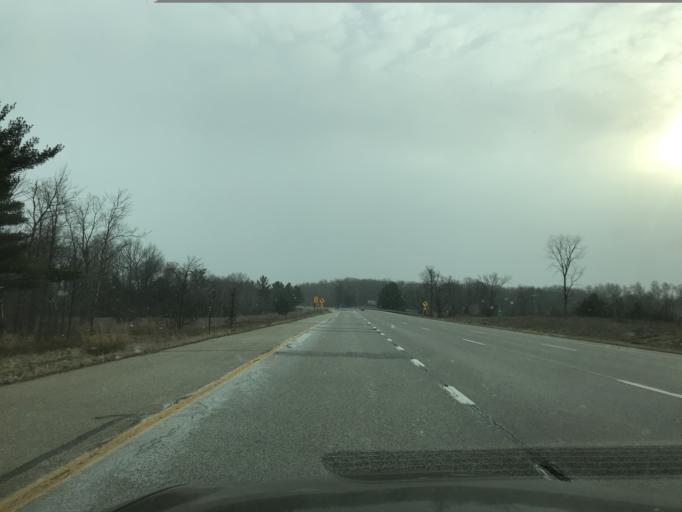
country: US
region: Michigan
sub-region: Clare County
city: Clare
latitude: 43.8558
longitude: -84.7789
